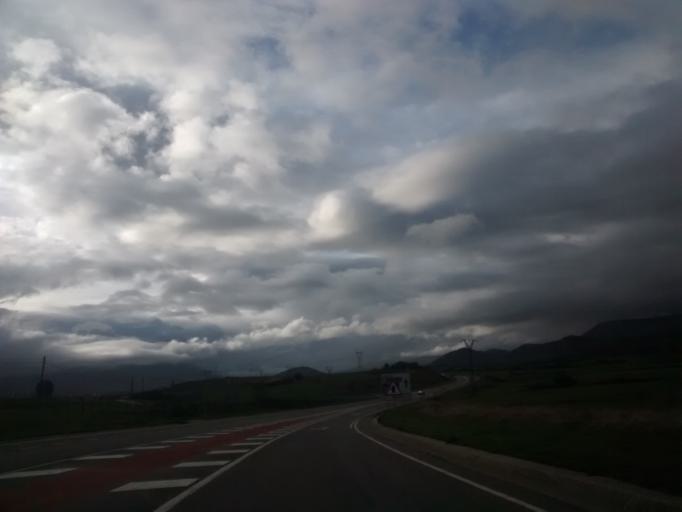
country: ES
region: Cantabria
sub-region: Provincia de Cantabria
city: Reinosa
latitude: 43.0053
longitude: -4.1010
